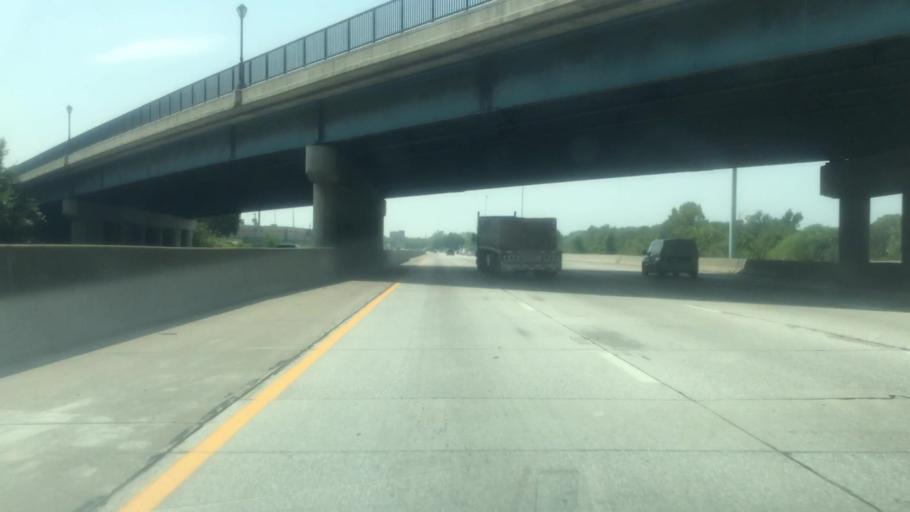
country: US
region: Kansas
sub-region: Johnson County
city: Merriam
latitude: 39.0347
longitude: -94.6862
